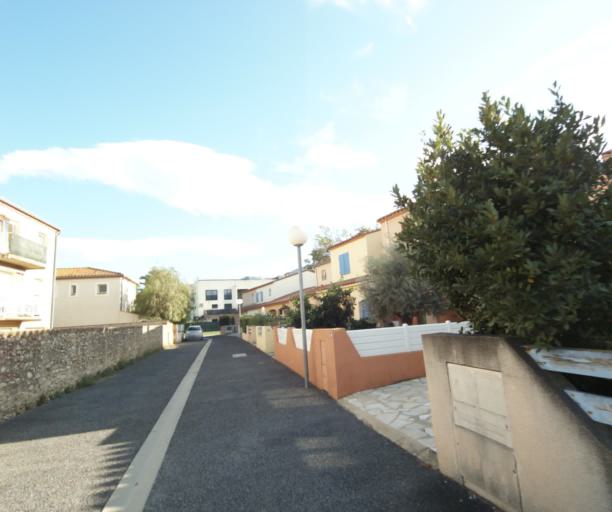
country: FR
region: Languedoc-Roussillon
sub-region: Departement des Pyrenees-Orientales
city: Argelers
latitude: 42.5462
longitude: 3.0277
